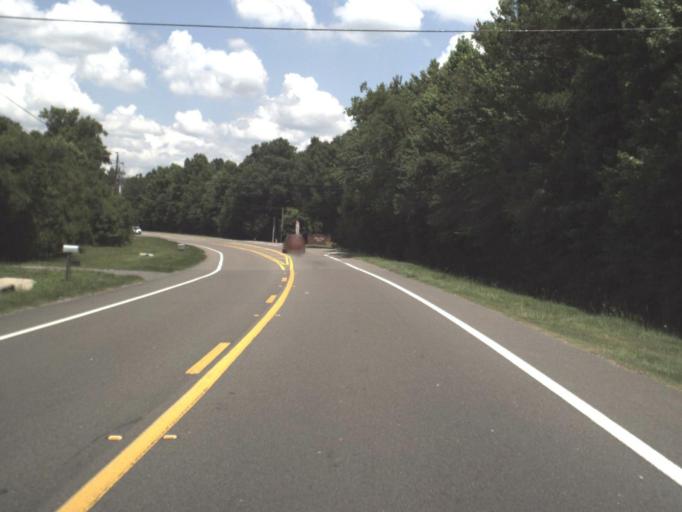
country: US
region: Florida
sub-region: Nassau County
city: Nassau Village-Ratliff
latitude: 30.5468
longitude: -81.7812
